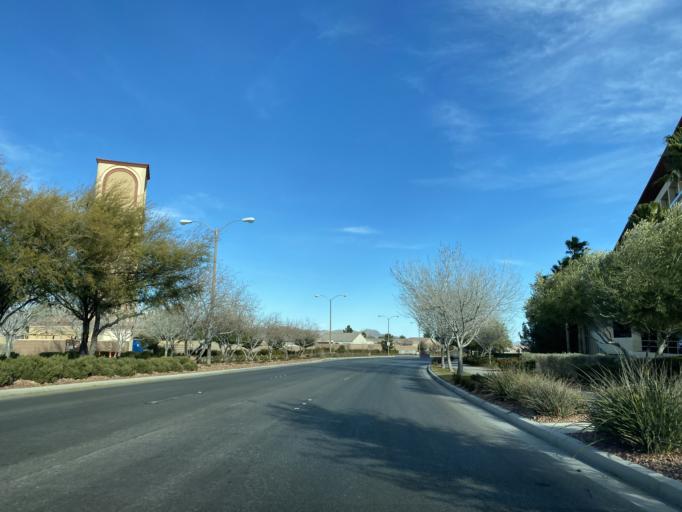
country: US
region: Nevada
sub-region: Clark County
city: North Las Vegas
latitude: 36.2944
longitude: -115.1808
